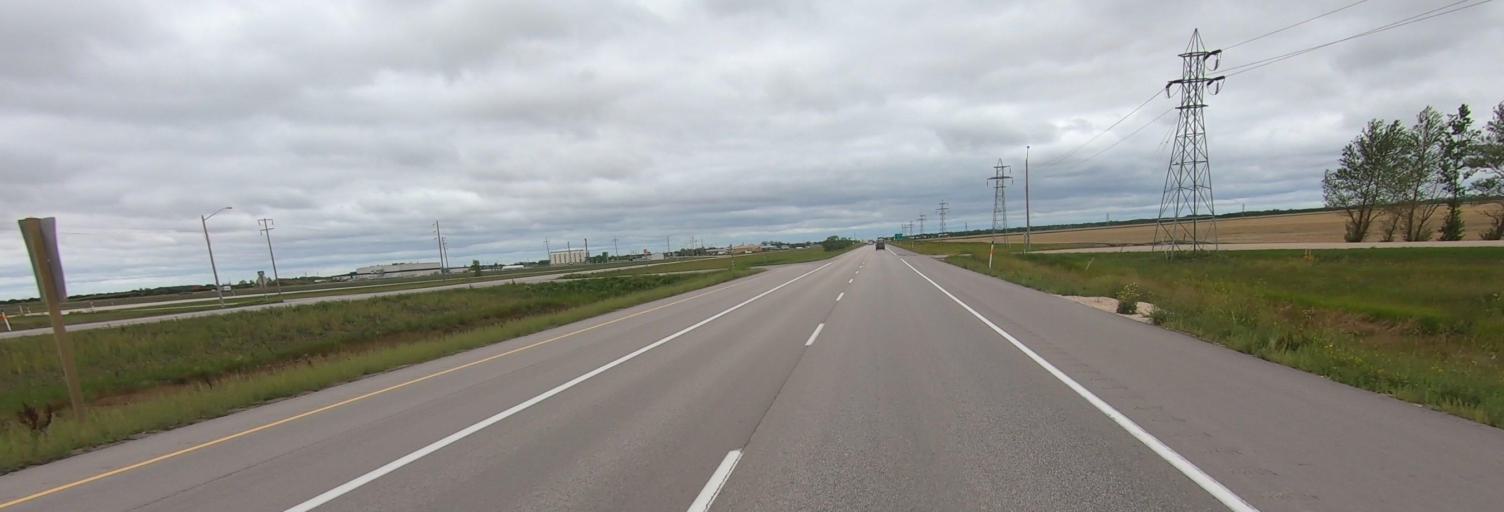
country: CA
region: Manitoba
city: Headingley
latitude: 49.9016
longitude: -97.7243
